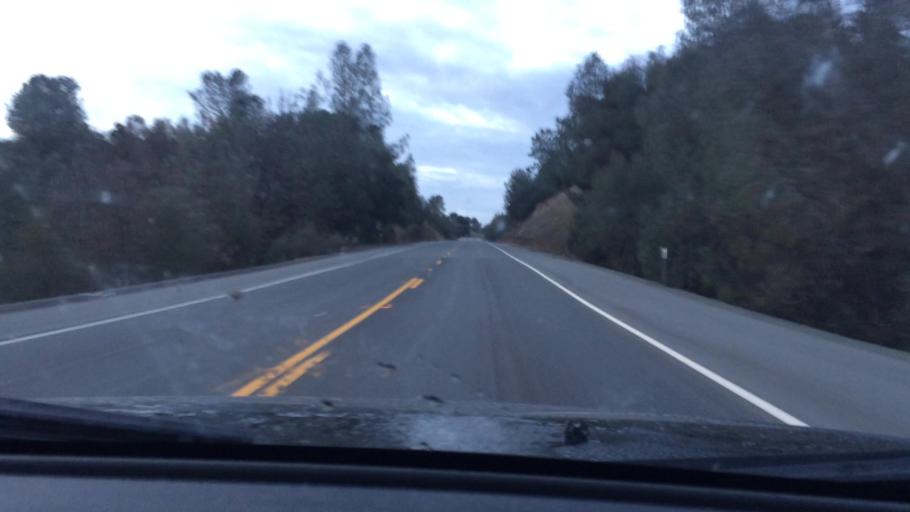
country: US
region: California
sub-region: Amador County
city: Ione
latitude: 38.4059
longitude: -120.8908
